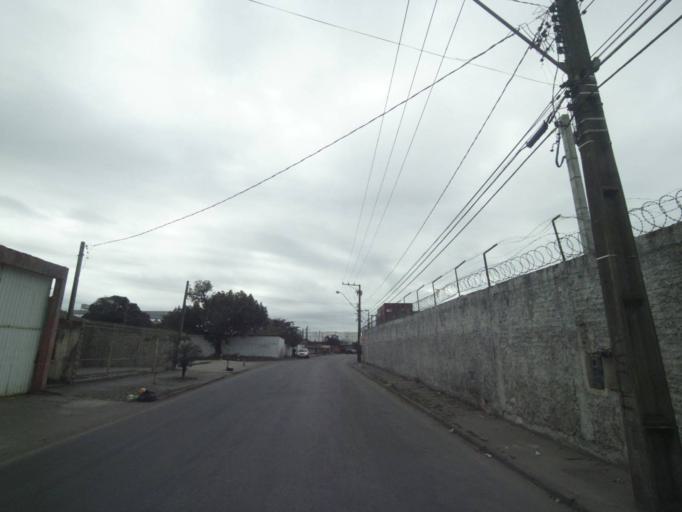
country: BR
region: Parana
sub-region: Paranagua
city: Paranagua
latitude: -25.5157
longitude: -48.5287
